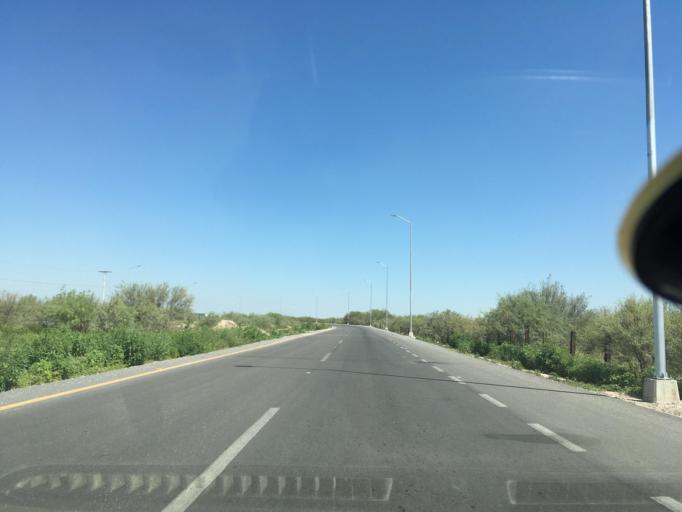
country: MX
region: Coahuila
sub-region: Torreon
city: Fraccionamiento la Noria
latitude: 25.4849
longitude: -103.3189
